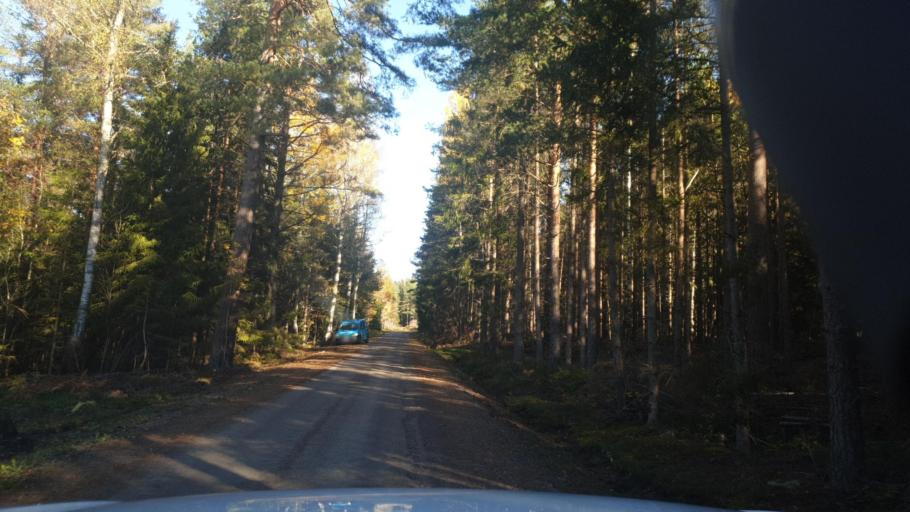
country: SE
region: Vaermland
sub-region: Arvika Kommun
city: Arvika
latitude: 59.5107
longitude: 12.7293
